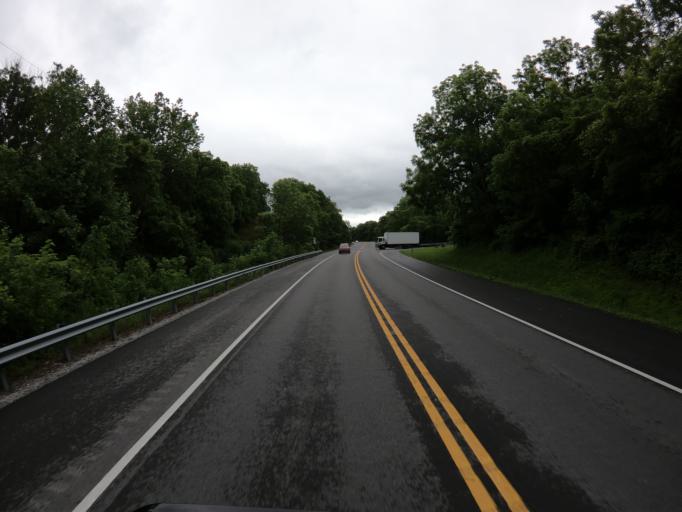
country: US
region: Maryland
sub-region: Washington County
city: Keedysville
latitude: 39.4669
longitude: -77.7220
